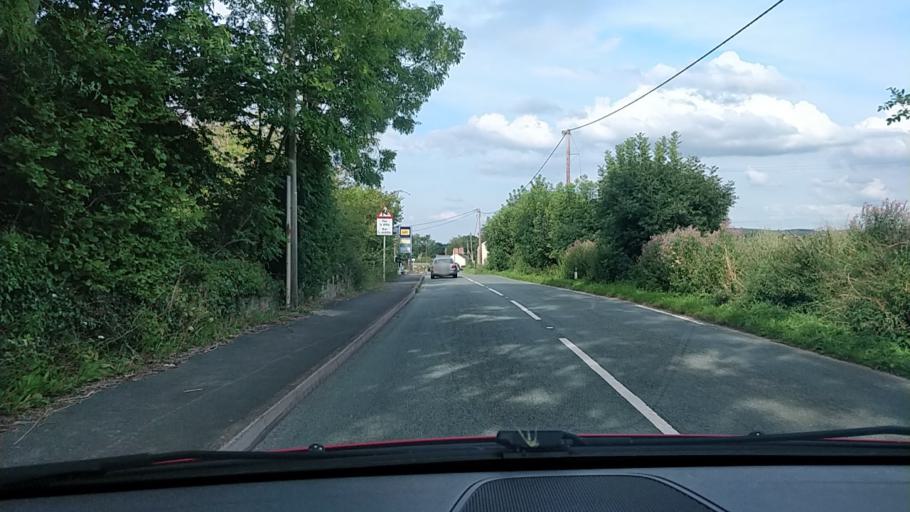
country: GB
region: Wales
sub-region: County of Flintshire
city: Leeswood
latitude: 53.1125
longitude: -3.1160
